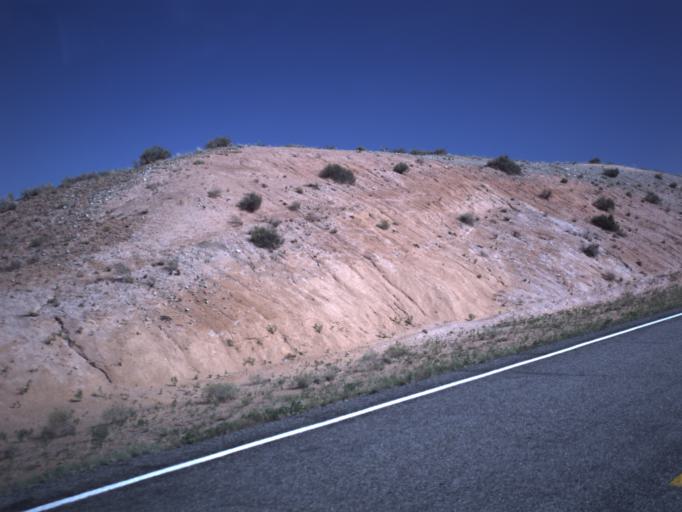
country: US
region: Utah
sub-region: Emery County
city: Ferron
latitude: 38.3298
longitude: -110.6798
